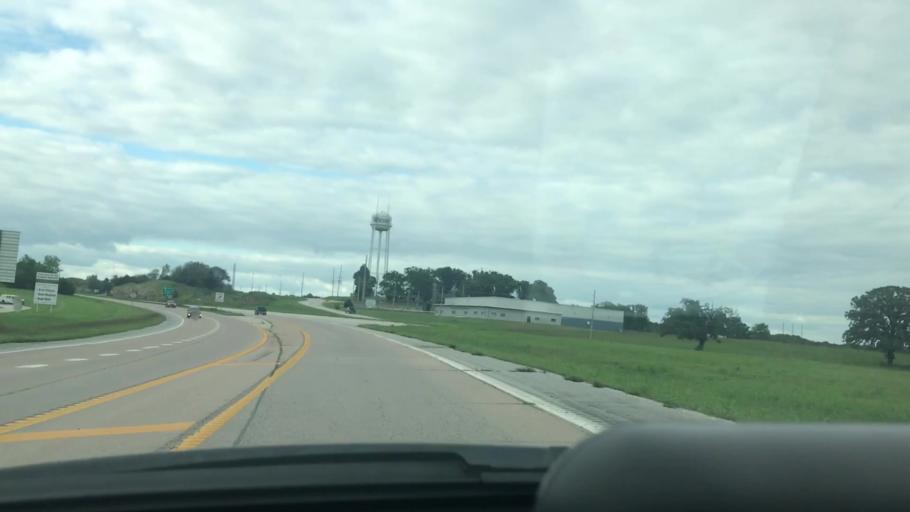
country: US
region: Missouri
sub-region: Benton County
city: Warsaw
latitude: 38.2450
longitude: -93.3603
